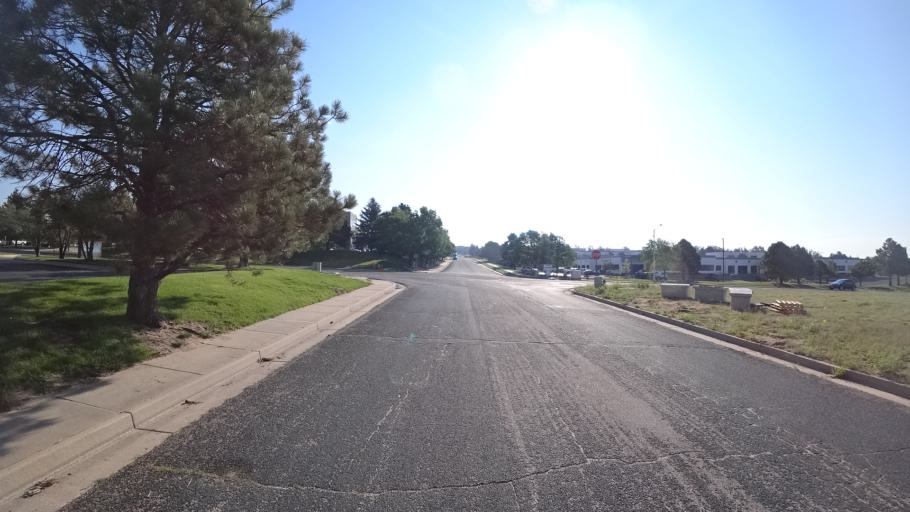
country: US
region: Colorado
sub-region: El Paso County
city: Air Force Academy
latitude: 38.9580
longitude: -104.7912
